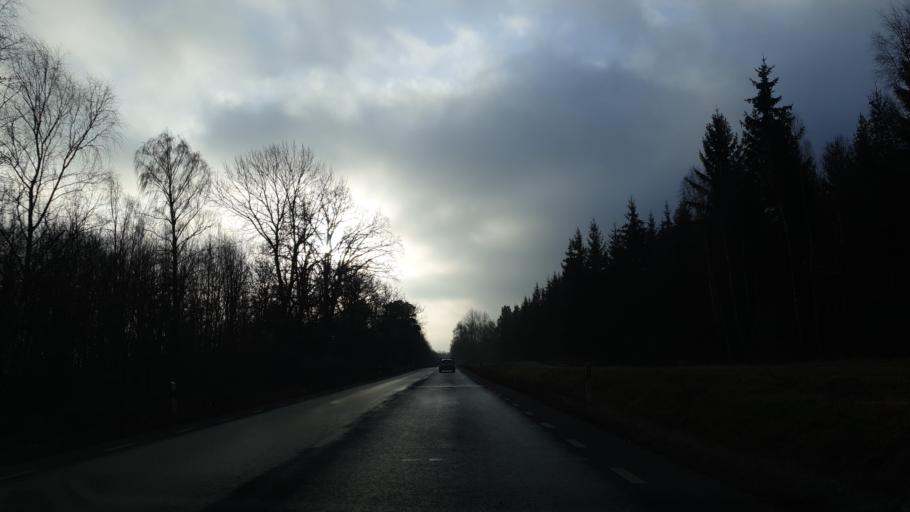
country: SE
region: Blekinge
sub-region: Karlshamns Kommun
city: Morrum
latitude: 56.1413
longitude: 14.6701
